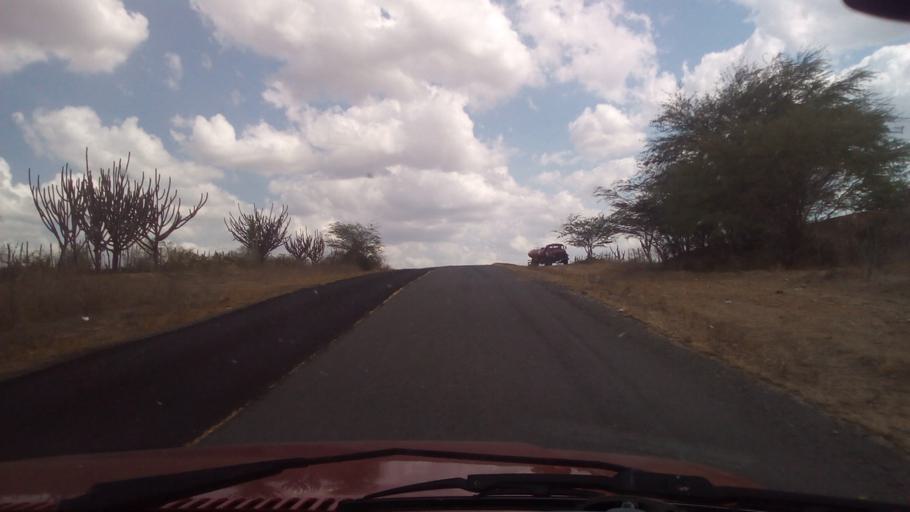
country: BR
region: Paraiba
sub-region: Bananeiras
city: Bananeiras
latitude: -6.7154
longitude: -35.7190
